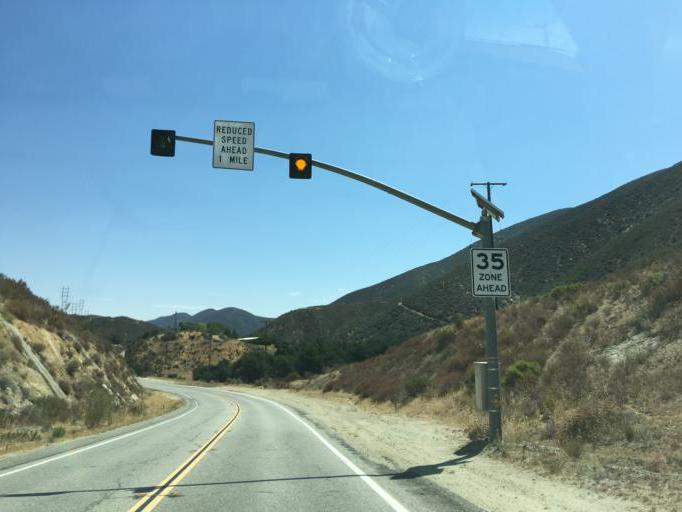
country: US
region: California
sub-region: Los Angeles County
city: Green Valley
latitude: 34.6105
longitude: -118.4400
